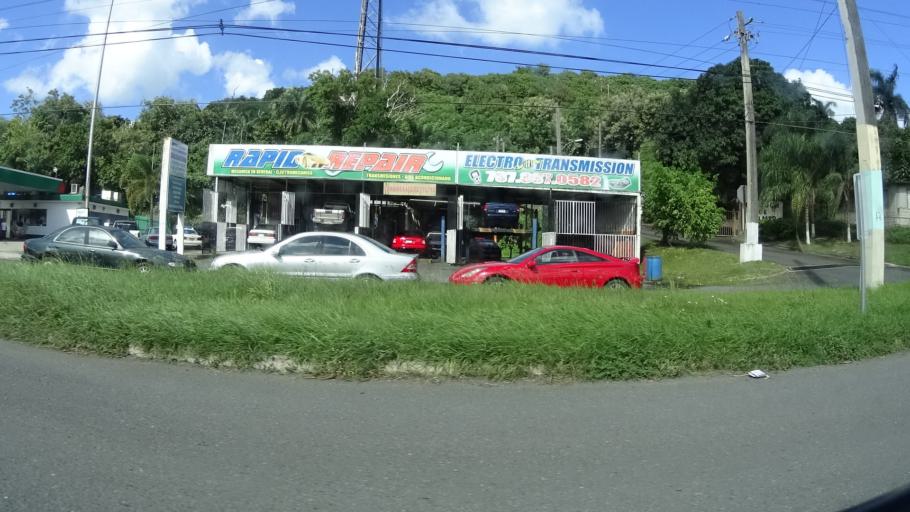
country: PR
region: Rio Grande
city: Palmer
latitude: 18.3717
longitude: -65.7727
